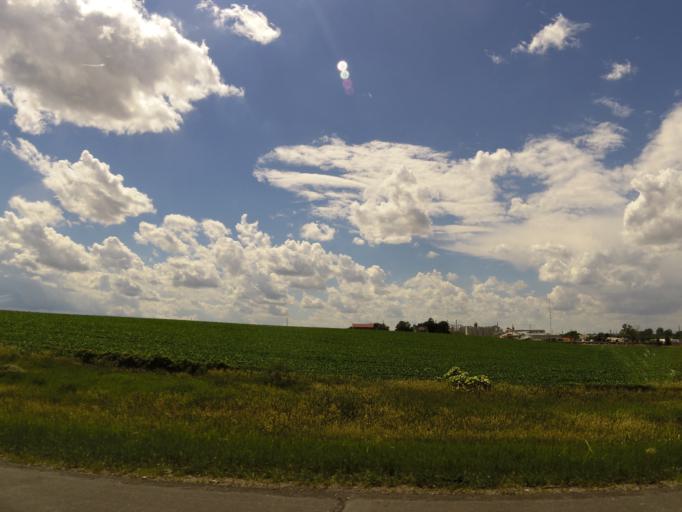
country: US
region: Iowa
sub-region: Linn County
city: Ely
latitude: 41.9111
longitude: -91.6719
